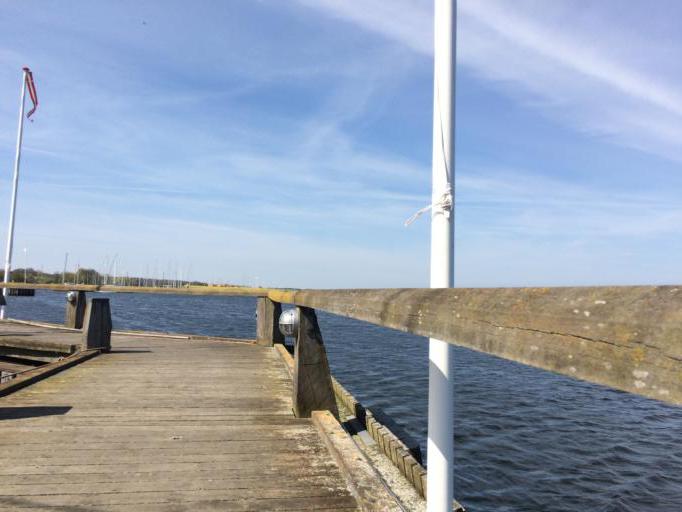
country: DK
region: Zealand
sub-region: Roskilde Kommune
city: Roskilde
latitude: 55.6511
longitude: 12.0799
